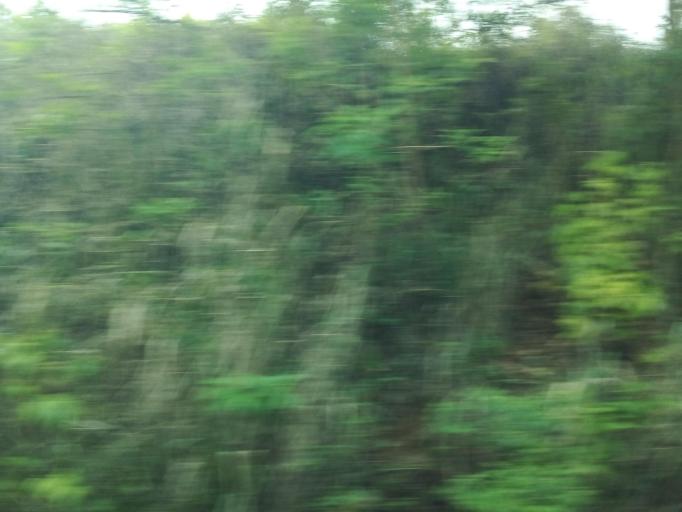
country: BR
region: Minas Gerais
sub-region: Nova Era
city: Nova Era
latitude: -19.6733
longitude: -42.8963
